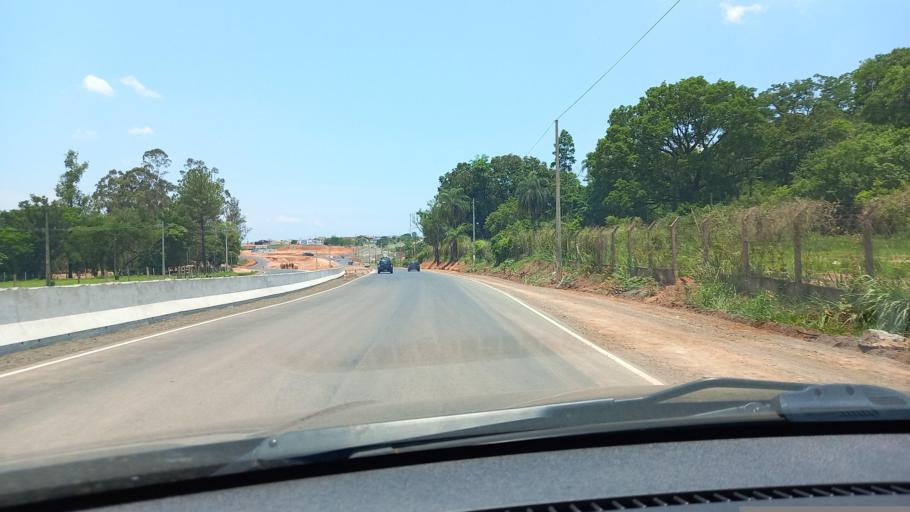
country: BR
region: Sao Paulo
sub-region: Itapira
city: Itapira
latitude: -22.4027
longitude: -46.8461
